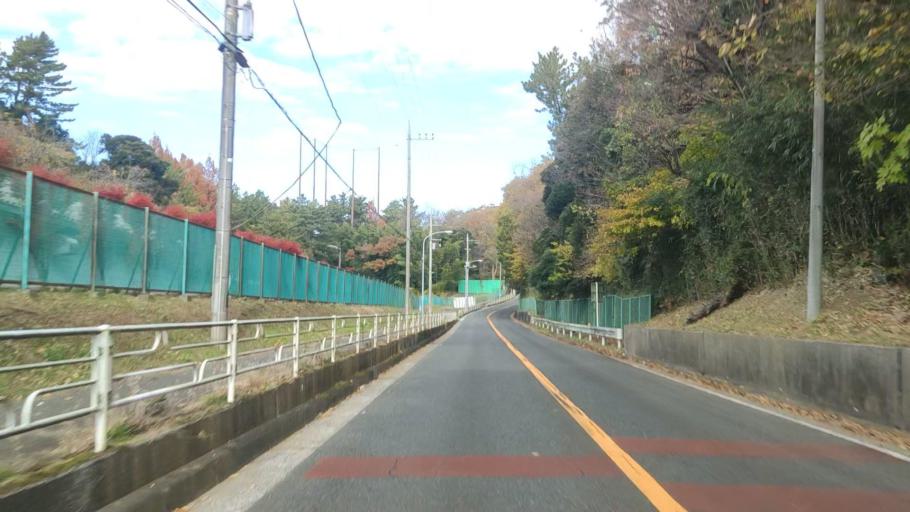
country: JP
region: Kanagawa
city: Yokohama
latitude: 35.4412
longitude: 139.5442
